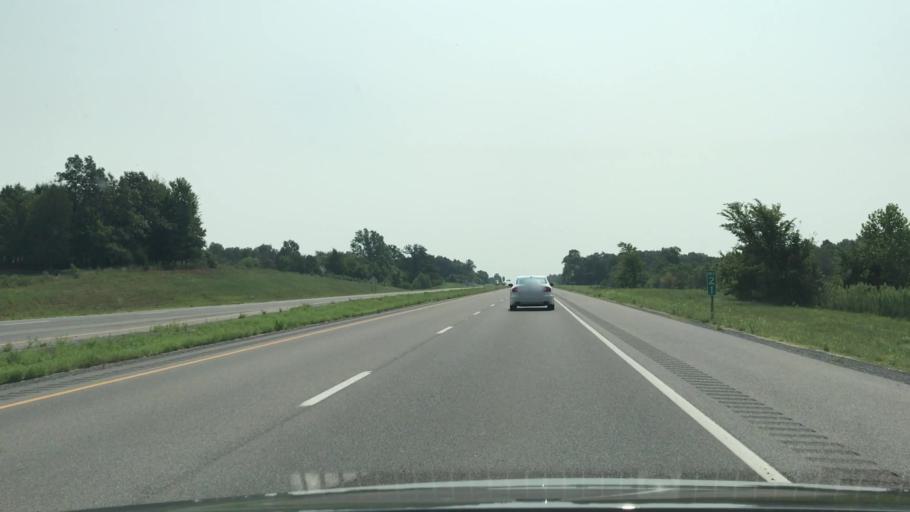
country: US
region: Kentucky
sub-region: Graves County
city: Mayfield
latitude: 36.6673
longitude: -88.4920
